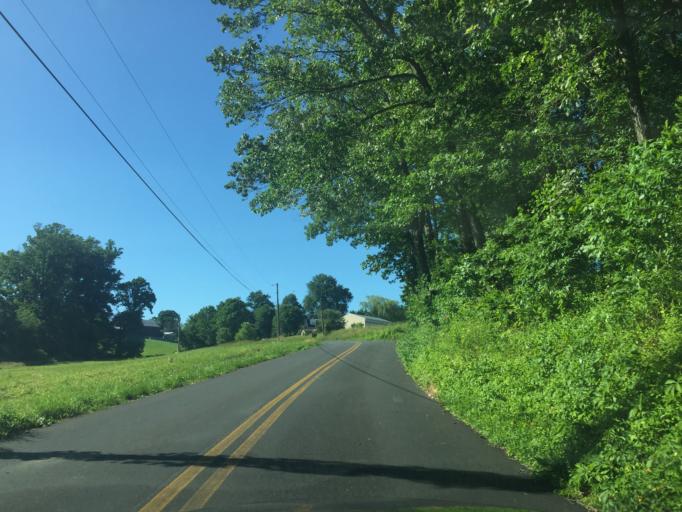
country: US
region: Maryland
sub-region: Carroll County
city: Westminster
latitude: 39.5628
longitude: -76.9197
